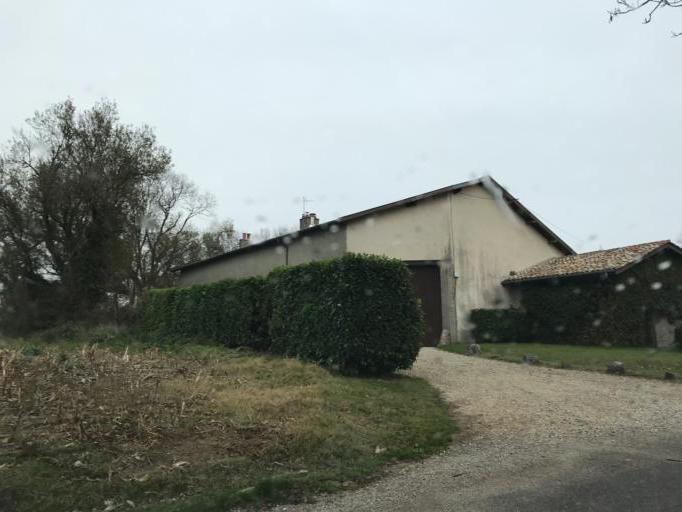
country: FR
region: Rhone-Alpes
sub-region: Departement de l'Ain
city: Saint-Maurice-de-Beynost
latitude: 45.8487
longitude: 4.9850
